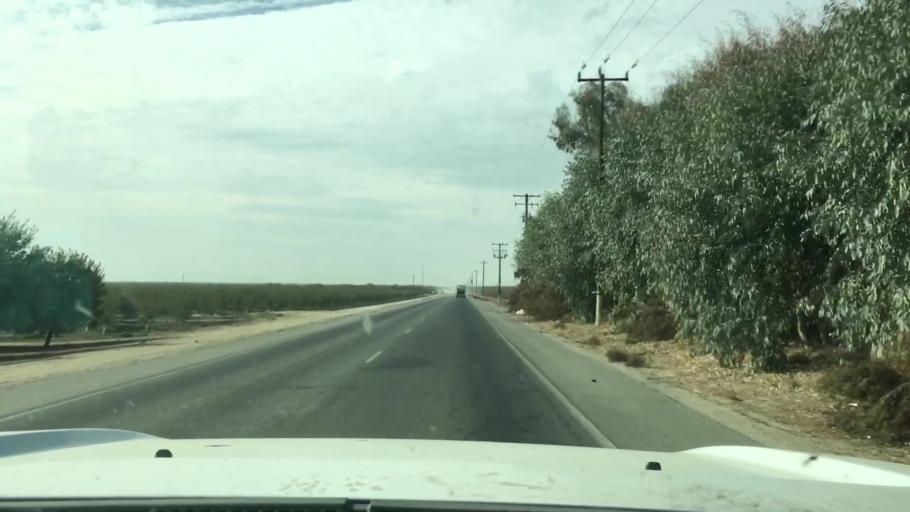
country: US
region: California
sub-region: Kern County
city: Buttonwillow
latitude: 35.5005
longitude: -119.4782
